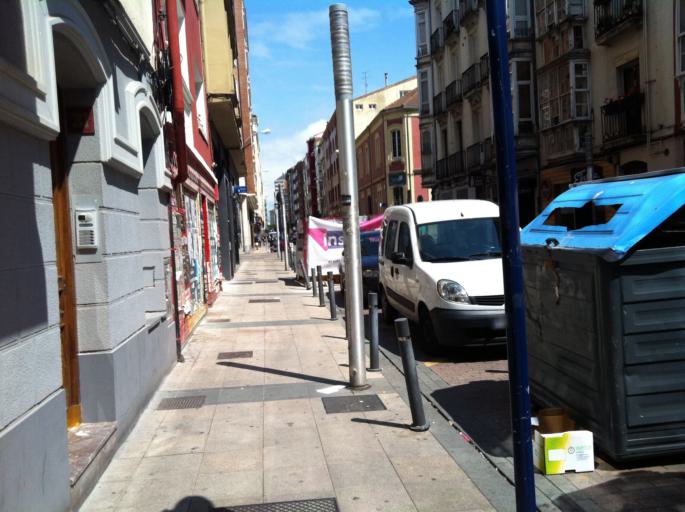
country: ES
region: Basque Country
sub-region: Provincia de Alava
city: Gasteiz / Vitoria
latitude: 42.8429
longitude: -2.6709
